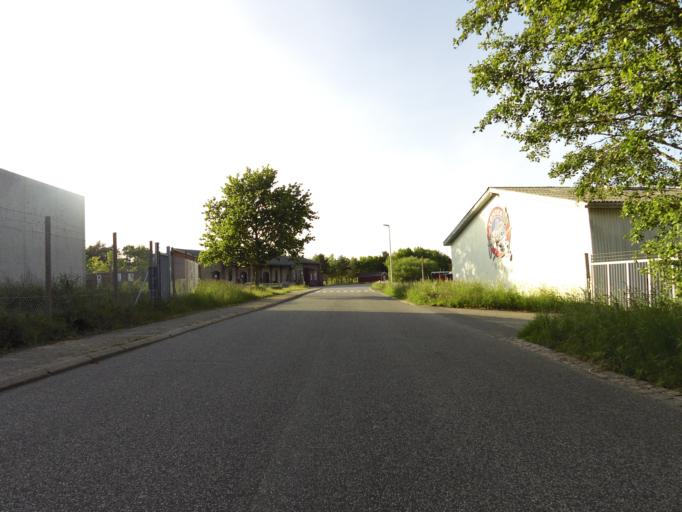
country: DK
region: South Denmark
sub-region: Tonder Kommune
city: Tonder
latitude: 54.9303
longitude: 8.8608
